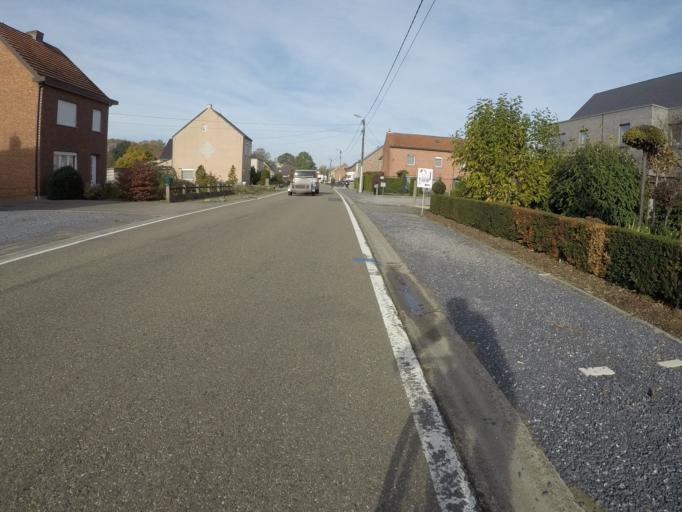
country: BE
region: Flanders
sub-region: Provincie Vlaams-Brabant
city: Begijnendijk
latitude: 51.0166
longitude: 4.7976
